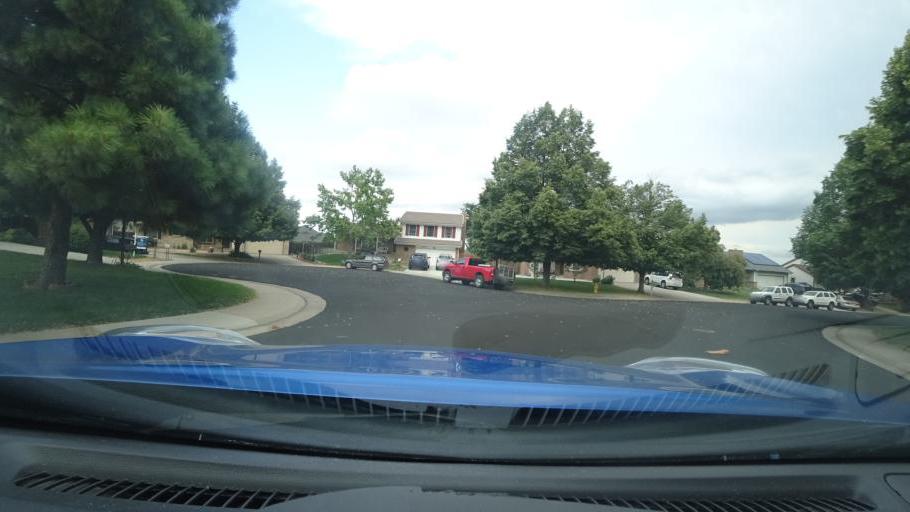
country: US
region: Colorado
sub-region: Adams County
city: Aurora
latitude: 39.6916
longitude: -104.8117
